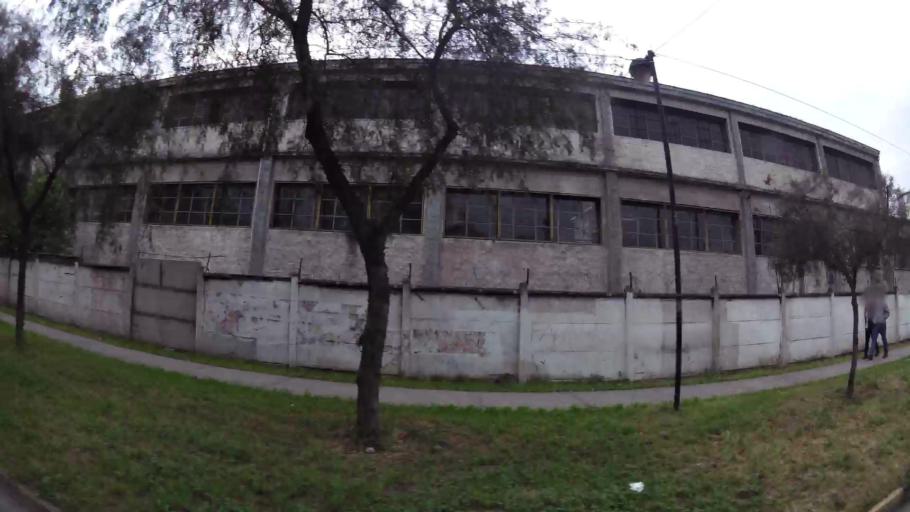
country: CL
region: Santiago Metropolitan
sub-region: Provincia de Santiago
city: Santiago
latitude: -33.4747
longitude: -70.6181
